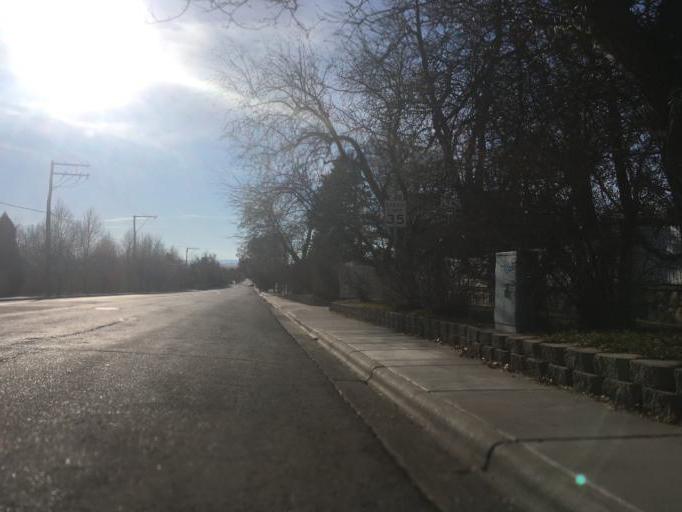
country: US
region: Montana
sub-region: Yellowstone County
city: Billings
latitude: 45.7945
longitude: -108.5592
